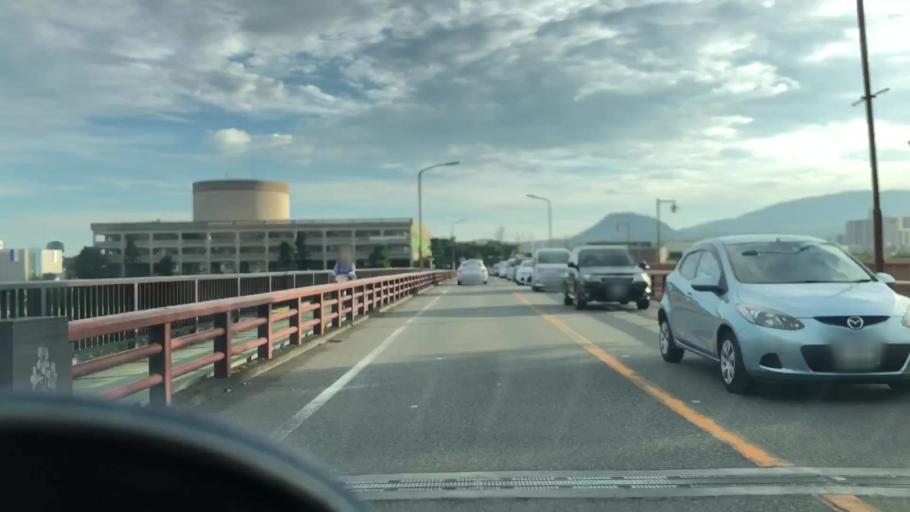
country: JP
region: Hyogo
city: Takarazuka
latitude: 34.8020
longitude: 135.3616
